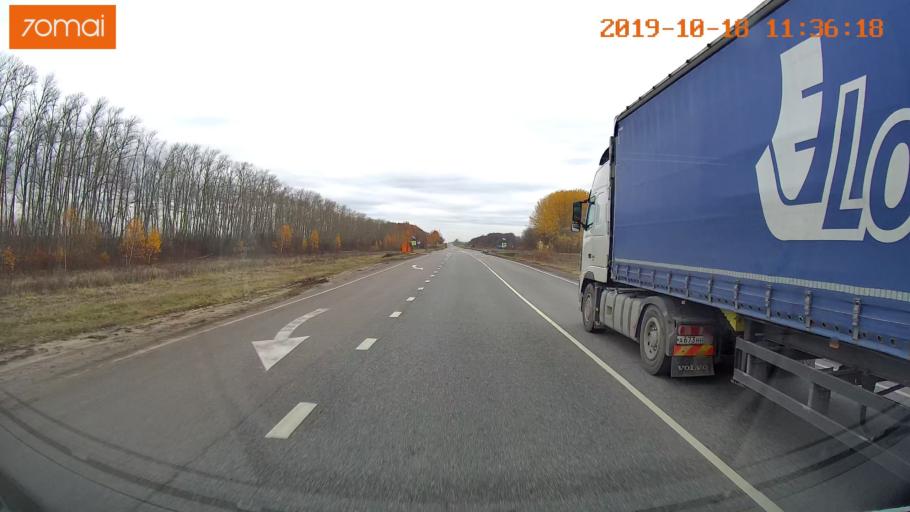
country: RU
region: Rjazan
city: Oktyabr'skiy
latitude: 54.1393
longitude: 38.8035
